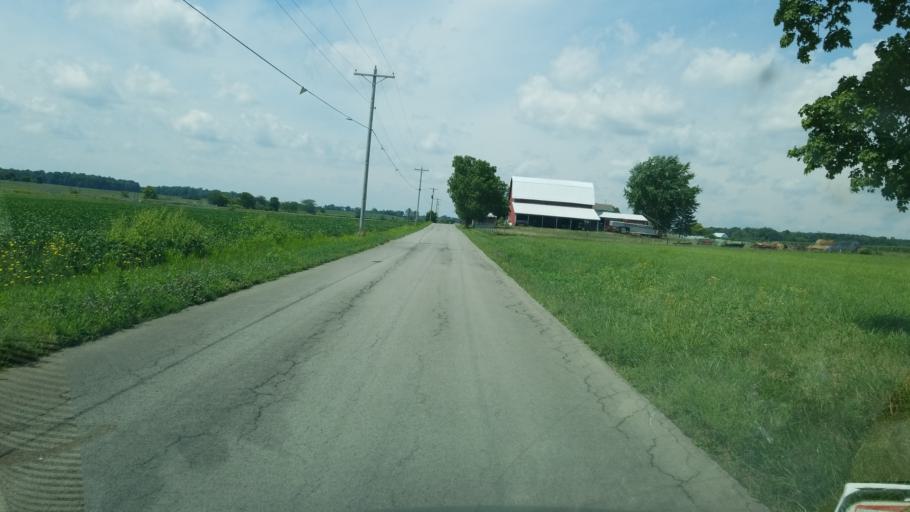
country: US
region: Ohio
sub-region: Hardin County
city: Forest
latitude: 40.8726
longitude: -83.5193
